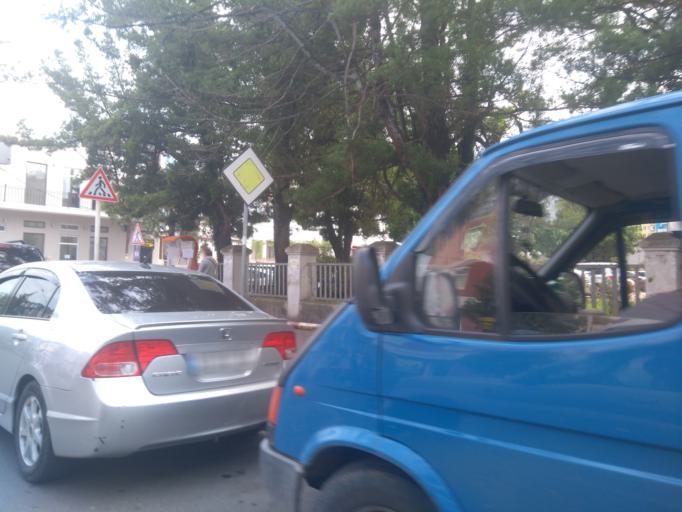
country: GE
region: Ajaria
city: Batumi
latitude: 41.6423
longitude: 41.6355
